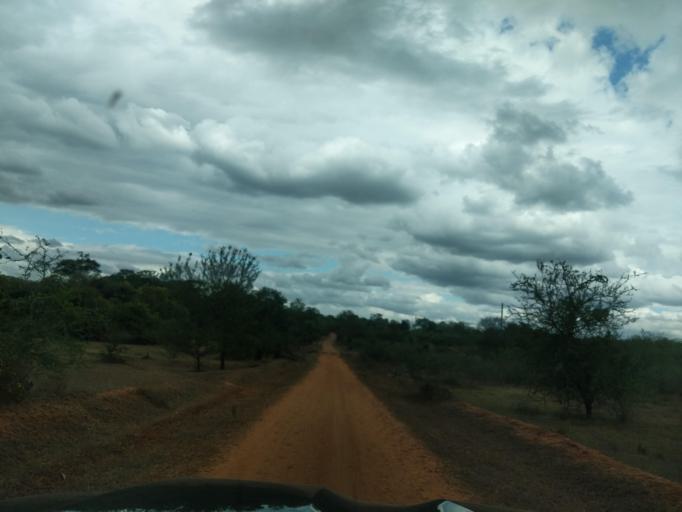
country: TZ
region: Pwani
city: Mvomero
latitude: -5.9365
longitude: 38.4207
